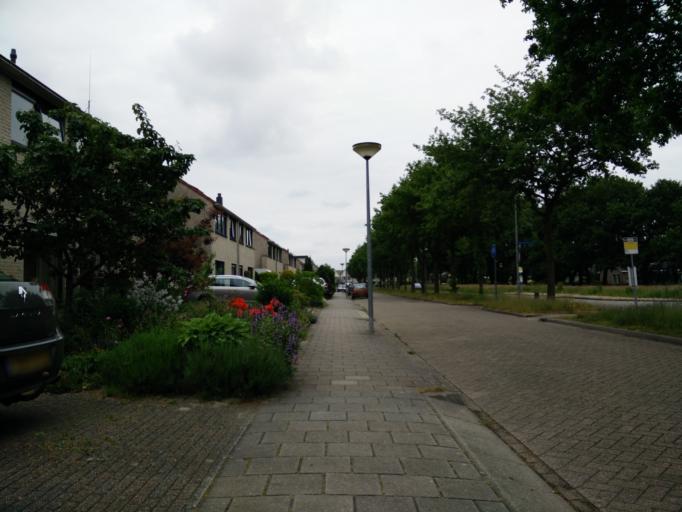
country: NL
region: Drenthe
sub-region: Gemeente Assen
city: Assen
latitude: 53.0181
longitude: 6.5950
